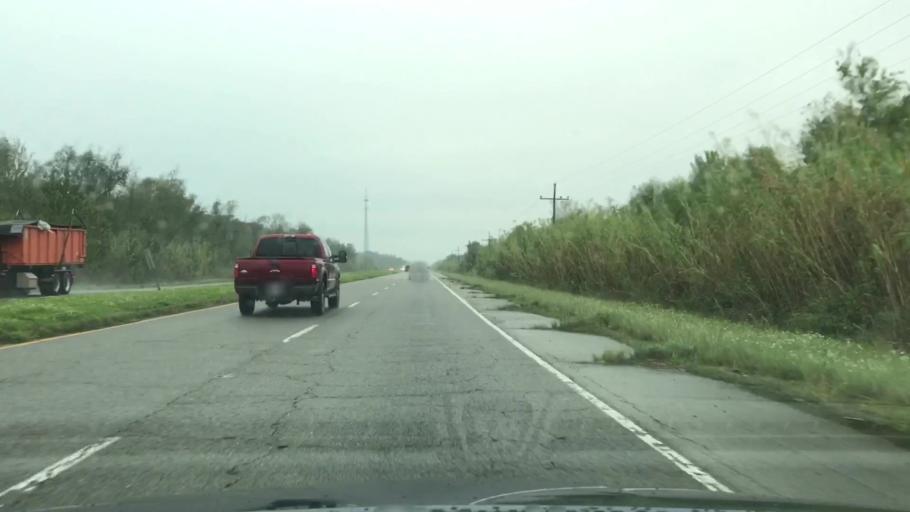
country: US
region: Louisiana
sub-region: Saint Charles Parish
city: Des Allemands
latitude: 29.7887
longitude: -90.5152
